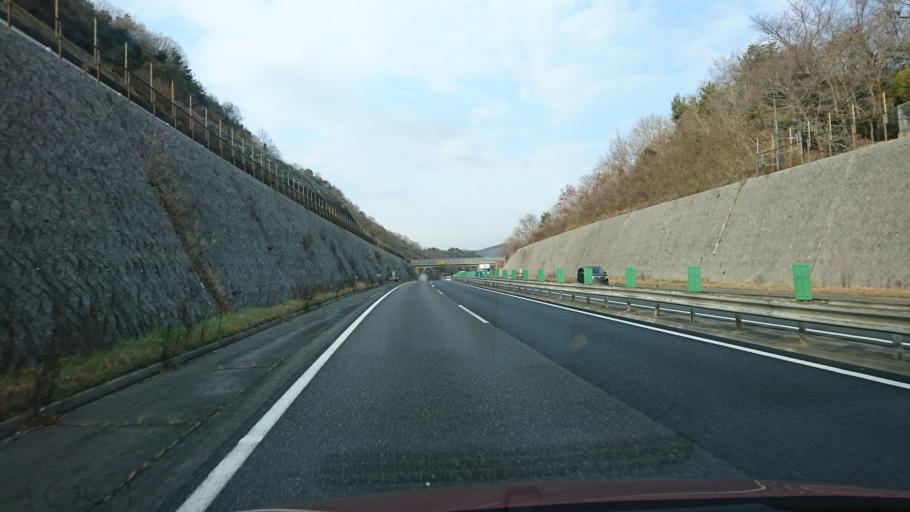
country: JP
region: Hyogo
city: Kariya
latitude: 34.7786
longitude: 134.2352
